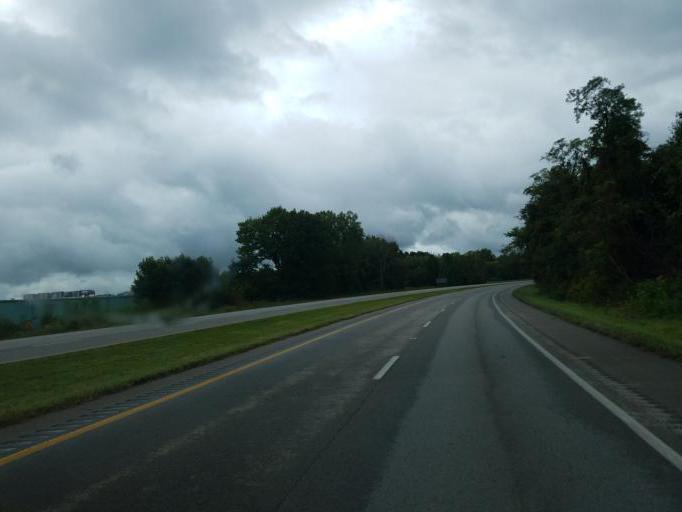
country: US
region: Ohio
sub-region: Scioto County
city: Wheelersburg
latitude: 38.7146
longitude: -82.8594
